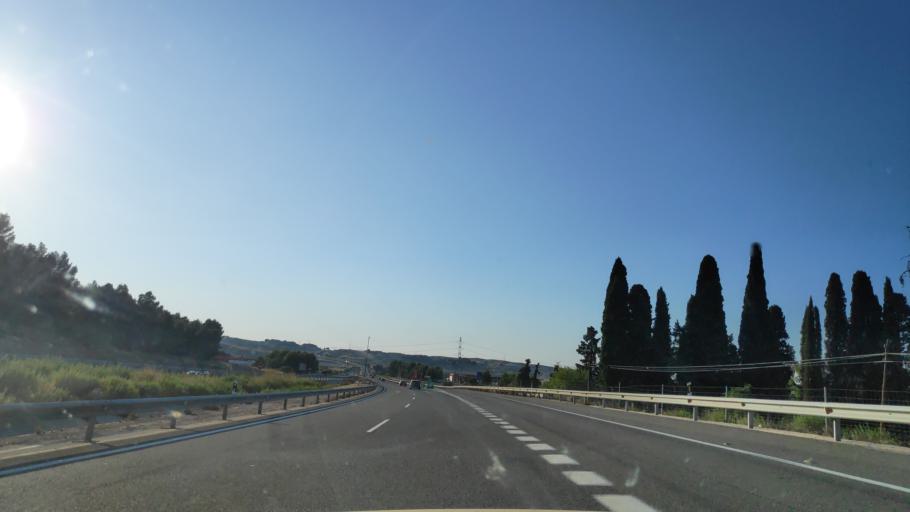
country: ES
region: Castille-La Mancha
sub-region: Provincia de Cuenca
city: Belinchon
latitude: 40.0295
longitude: -3.0378
